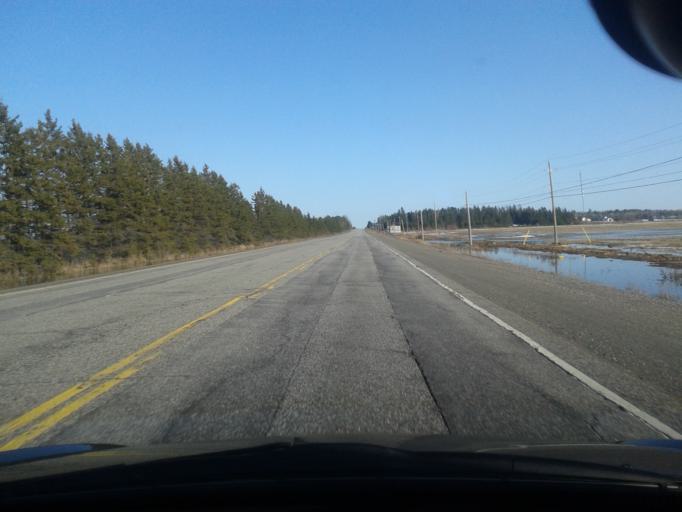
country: CA
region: Ontario
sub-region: Nipissing District
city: North Bay
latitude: 46.4017
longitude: -80.0262
